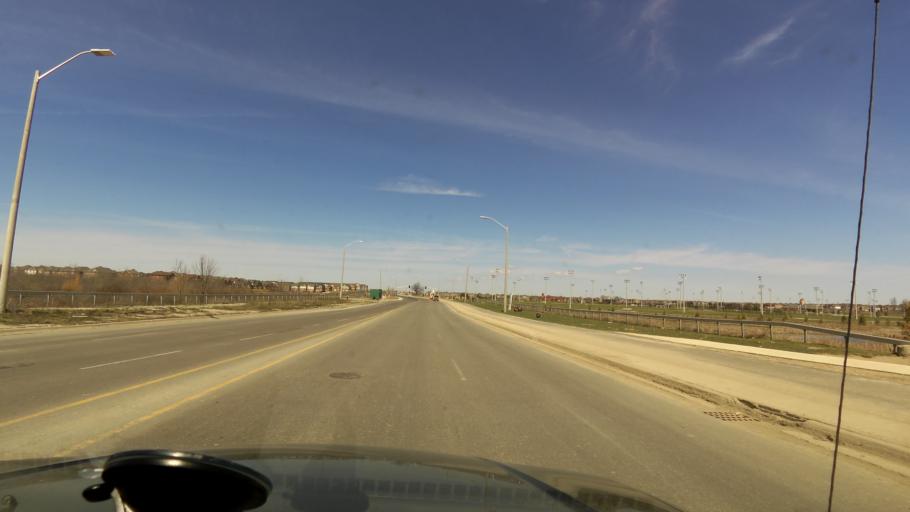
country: CA
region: Ontario
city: Brampton
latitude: 43.6824
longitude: -79.8416
